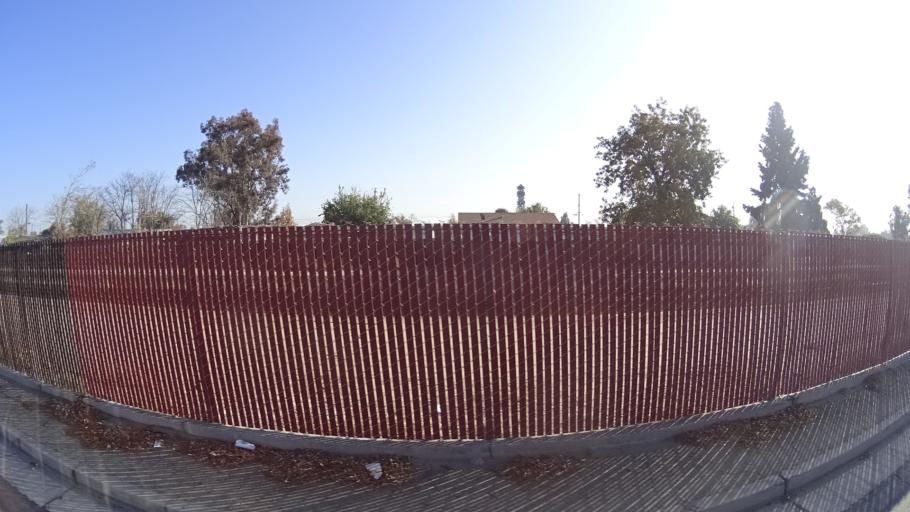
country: US
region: California
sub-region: Kern County
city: Bakersfield
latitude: 35.3373
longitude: -119.0212
